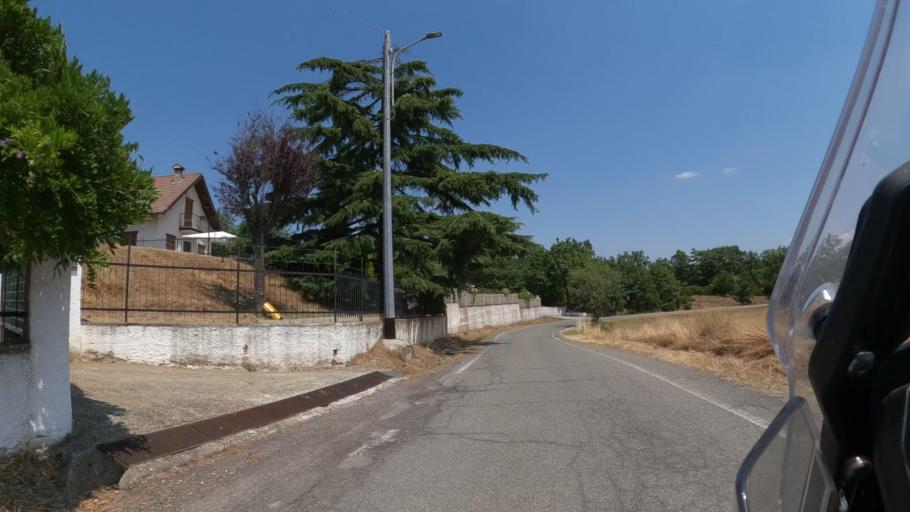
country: IT
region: Piedmont
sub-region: Provincia di Alessandria
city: Morbello
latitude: 44.5742
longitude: 8.5222
